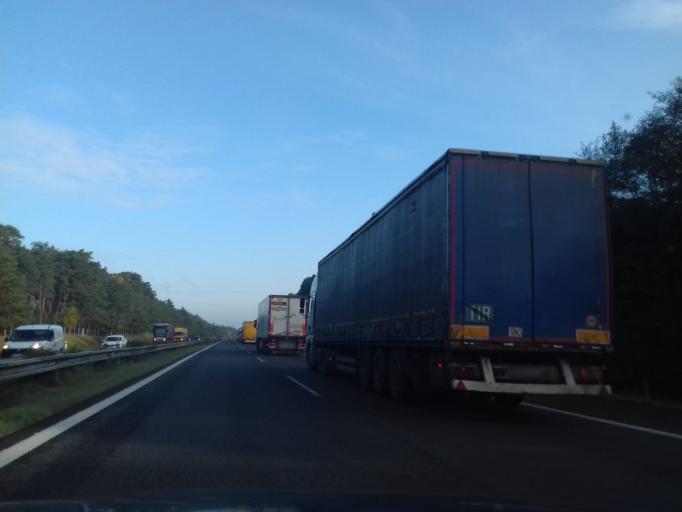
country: SK
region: Bratislavsky
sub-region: Okres Malacky
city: Malacky
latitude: 48.3977
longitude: 17.0281
